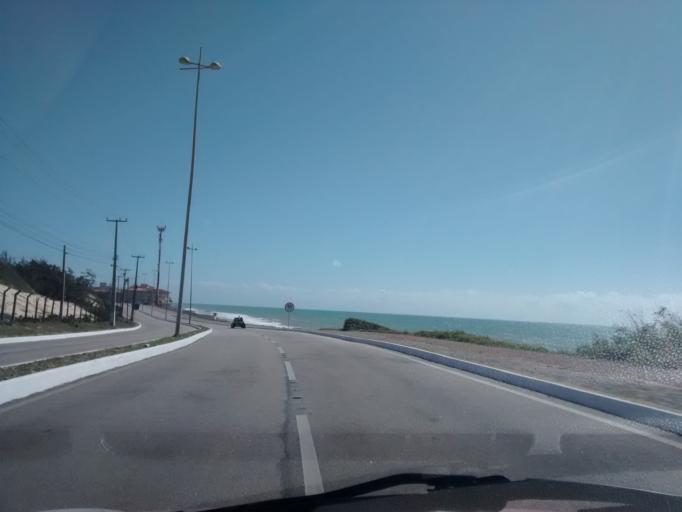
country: BR
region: Rio Grande do Norte
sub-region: Natal
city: Natal
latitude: -5.8149
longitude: -35.1823
